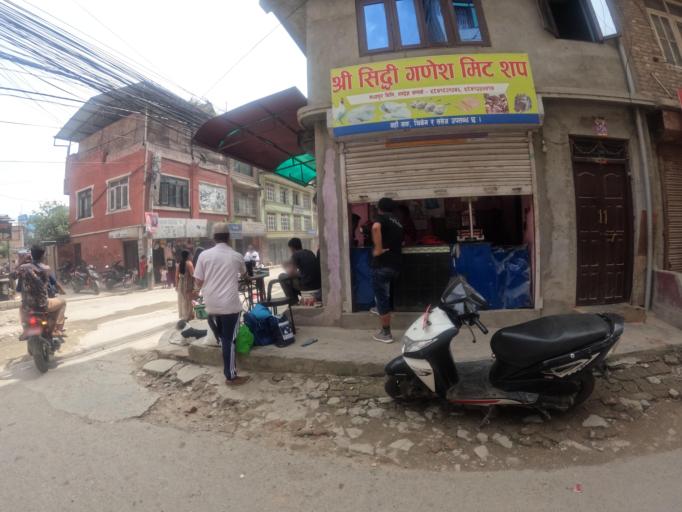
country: NP
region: Central Region
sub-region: Bagmati Zone
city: Bhaktapur
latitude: 27.6851
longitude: 85.3875
